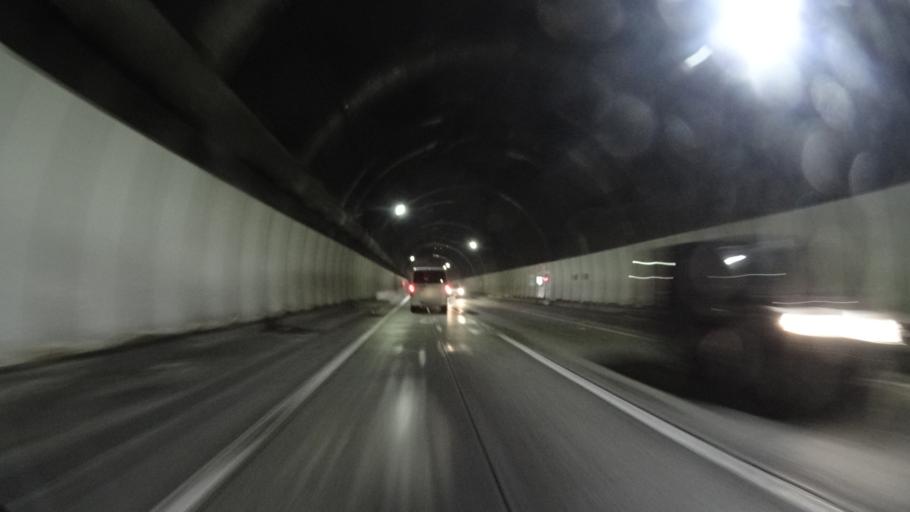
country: JP
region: Niigata
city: Joetsu
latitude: 37.1653
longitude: 138.2112
